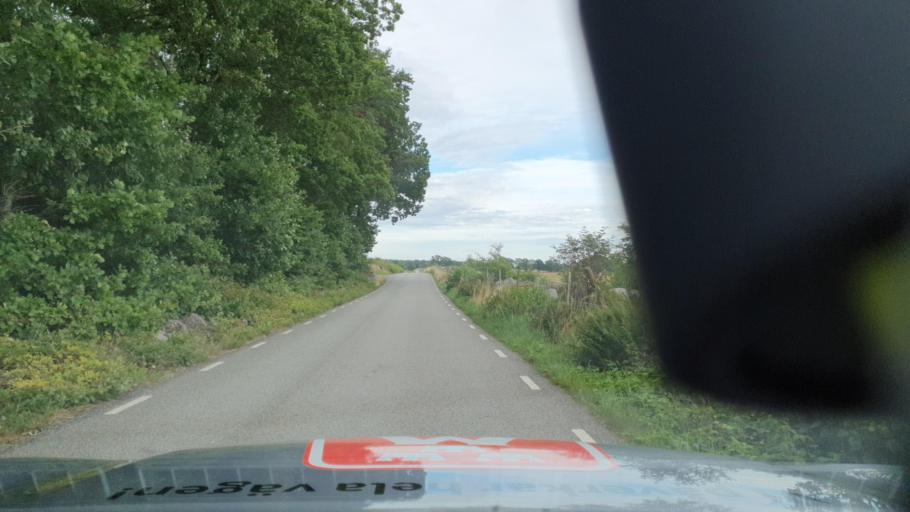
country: SE
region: Kalmar
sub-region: Kalmar Kommun
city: Lindsdal
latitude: 56.7761
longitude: 16.2587
